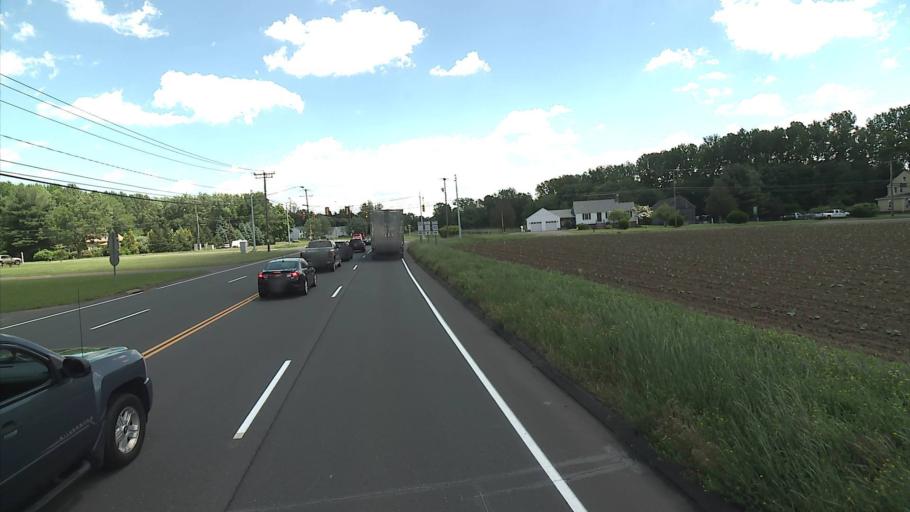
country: US
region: Connecticut
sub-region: Hartford County
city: Sherwood Manor
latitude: 42.0096
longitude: -72.5434
